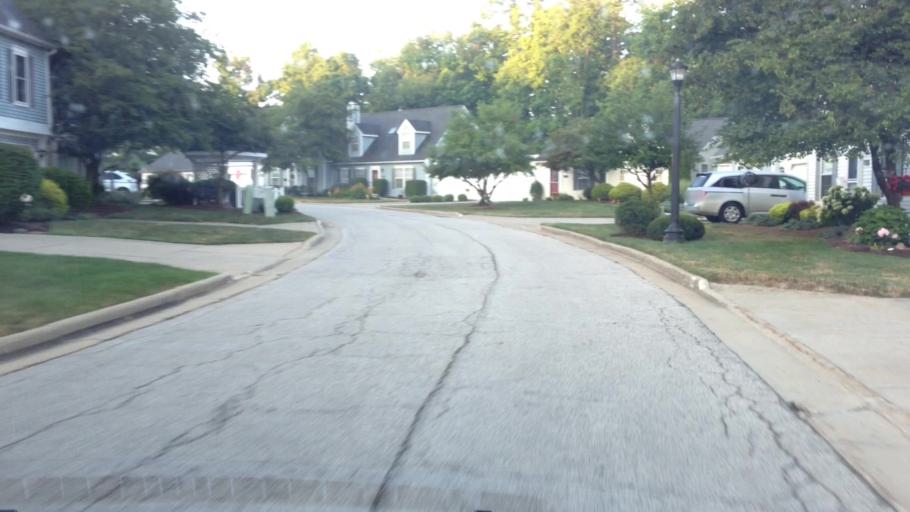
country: US
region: Ohio
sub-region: Summit County
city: Cuyahoga Falls
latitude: 41.1614
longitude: -81.4993
